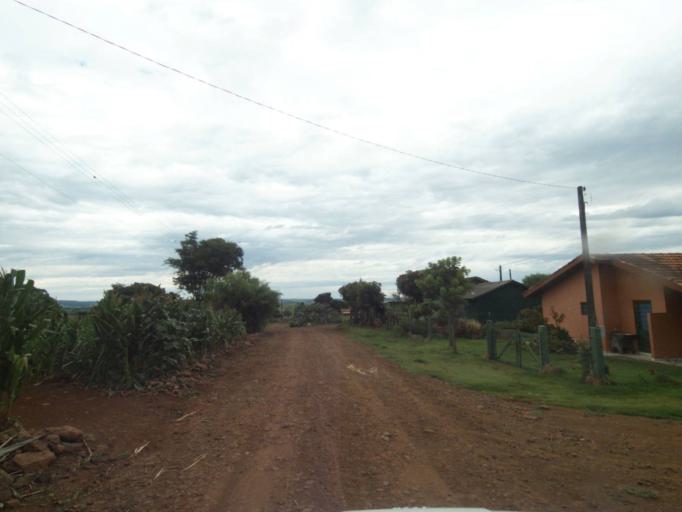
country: BR
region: Parana
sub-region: Guaraniacu
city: Guaraniacu
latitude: -24.9233
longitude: -52.9403
